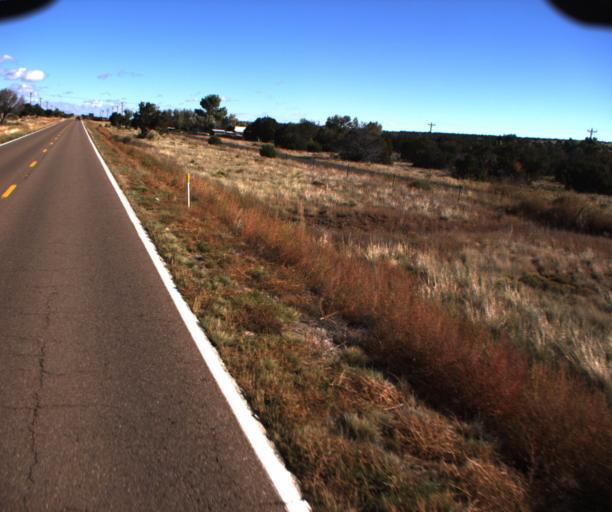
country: US
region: Arizona
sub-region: Apache County
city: Saint Johns
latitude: 34.4306
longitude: -109.6384
